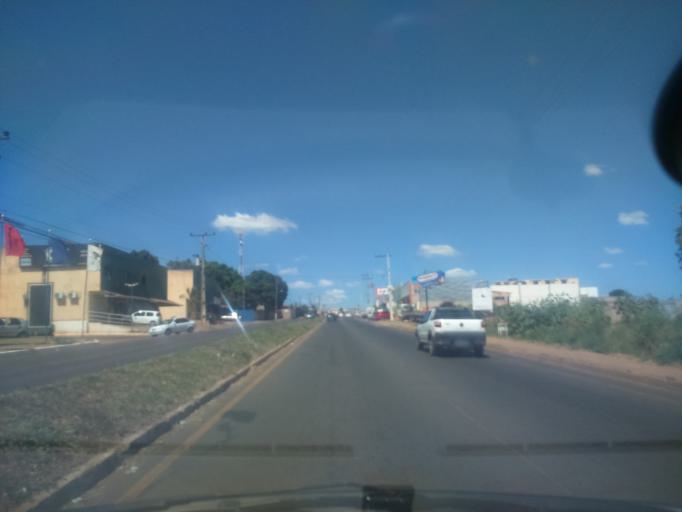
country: BR
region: Goias
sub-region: Luziania
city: Luziania
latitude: -16.1012
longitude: -47.9503
